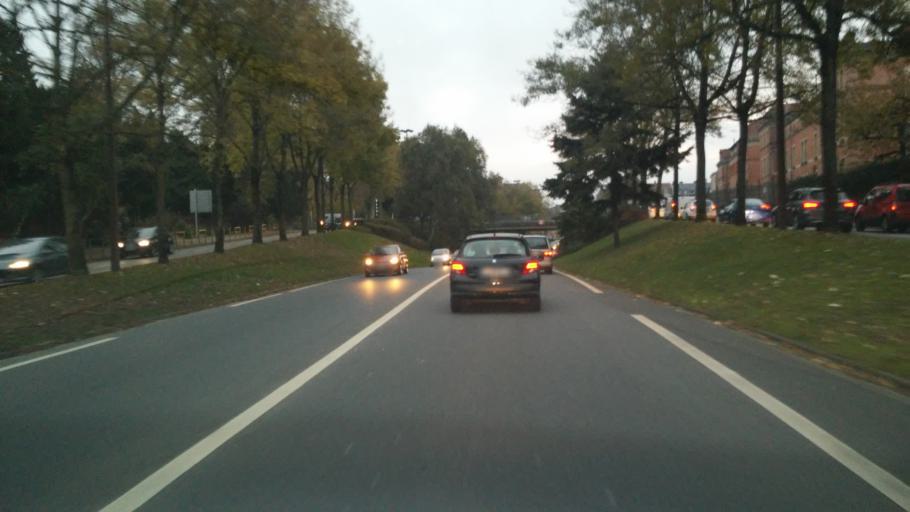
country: FR
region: Lorraine
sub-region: Departement de la Moselle
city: Metz
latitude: 49.1126
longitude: 6.1670
